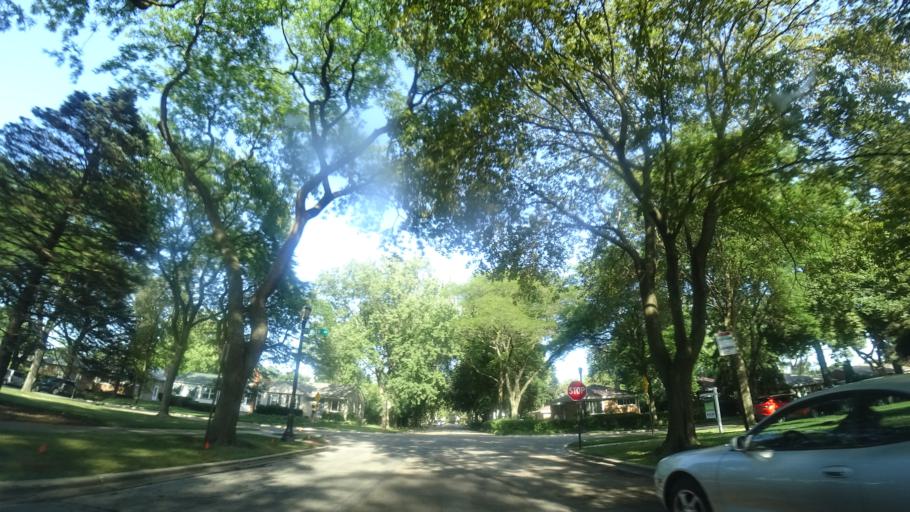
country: US
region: Illinois
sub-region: Cook County
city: Evanston
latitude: 42.0392
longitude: -87.7073
